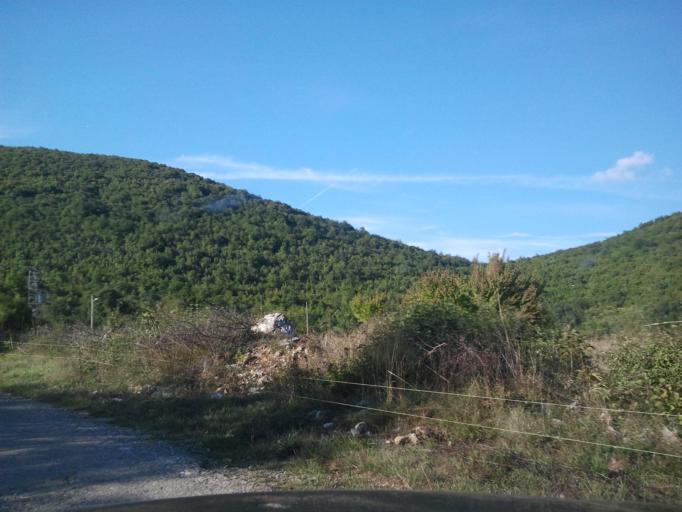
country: HR
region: Zadarska
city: Gracac
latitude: 44.3604
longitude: 15.7180
